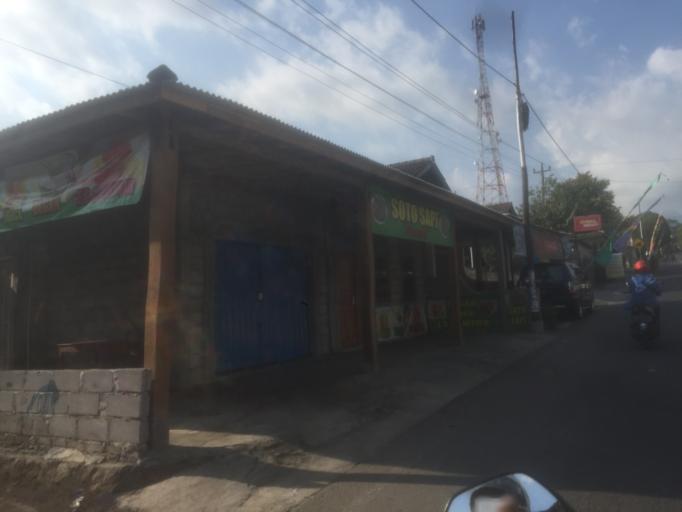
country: ID
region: Daerah Istimewa Yogyakarta
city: Sleman
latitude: -7.6597
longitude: 110.4214
